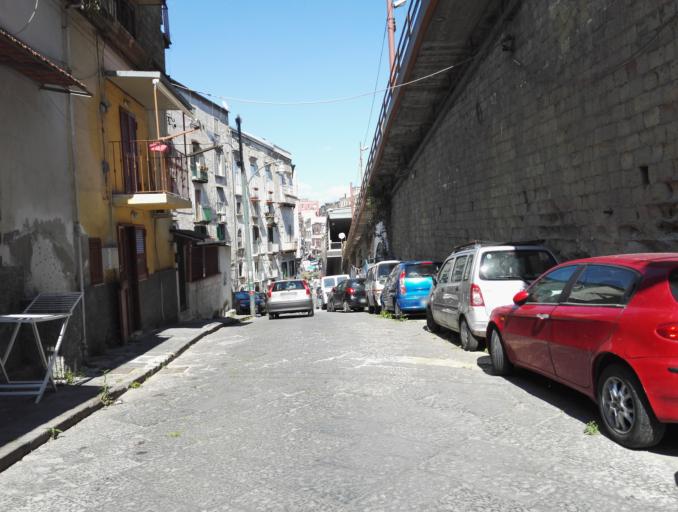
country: IT
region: Campania
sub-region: Provincia di Napoli
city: Napoli
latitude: 40.8469
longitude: 14.2439
